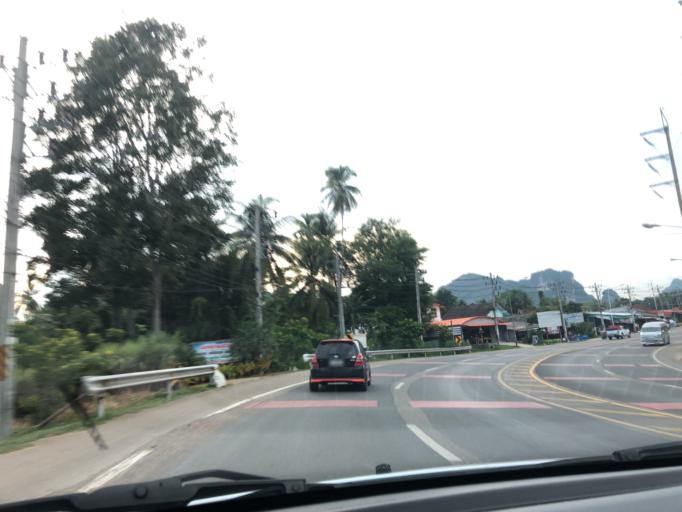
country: TH
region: Krabi
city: Krabi
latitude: 8.0805
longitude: 98.8691
